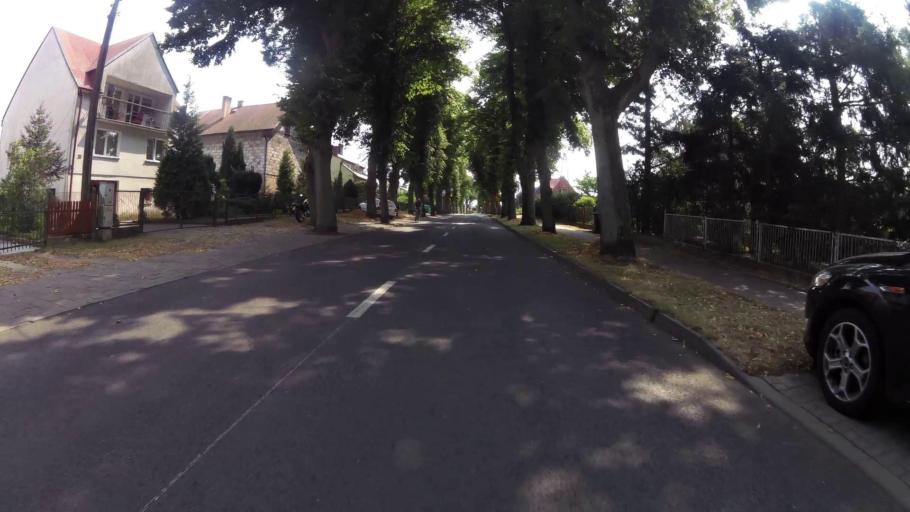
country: PL
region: West Pomeranian Voivodeship
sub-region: Powiat gryfinski
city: Moryn
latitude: 52.8500
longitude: 14.3966
